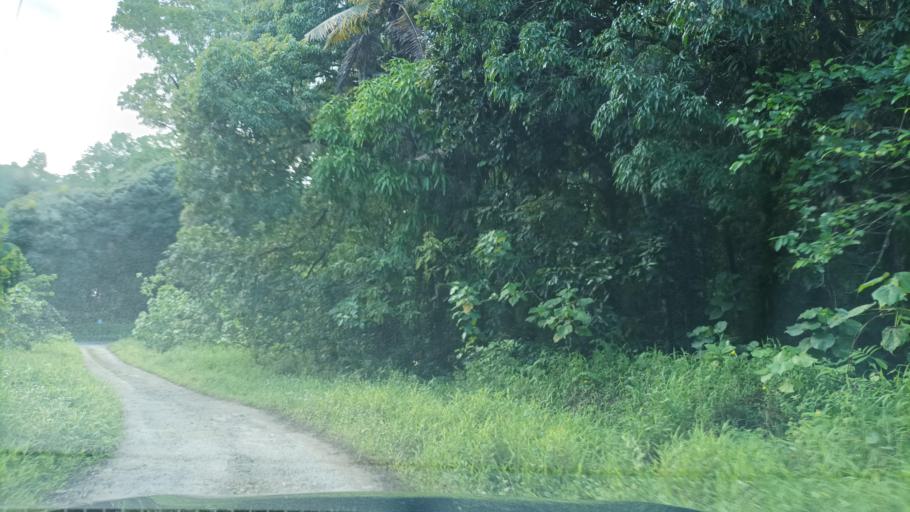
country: FM
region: Pohnpei
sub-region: Madolenihm Municipality
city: Madolenihm Municipality Government
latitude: 6.8463
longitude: 158.3168
